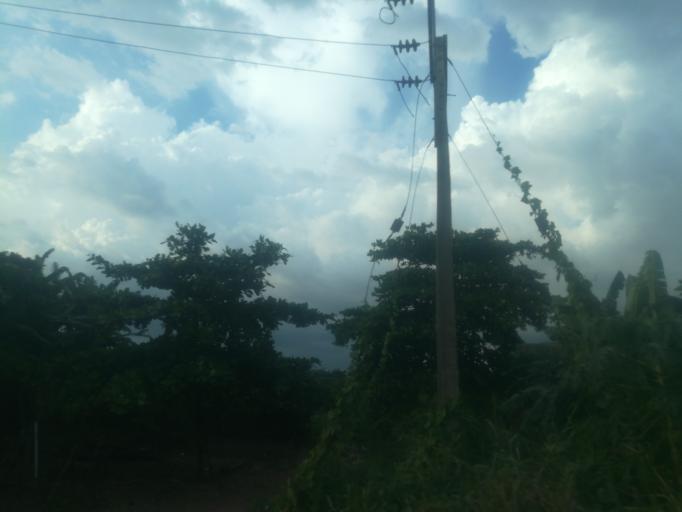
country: NG
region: Oyo
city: Ibadan
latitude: 7.3827
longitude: 3.8475
